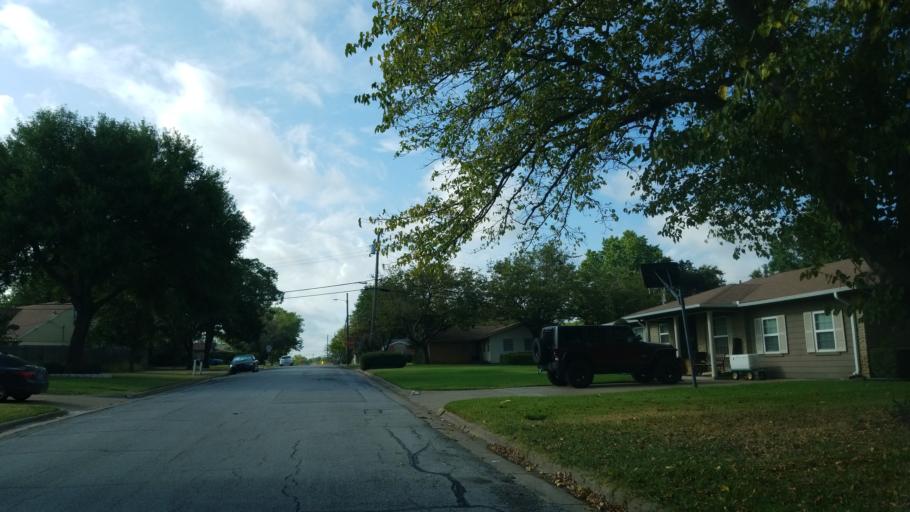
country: US
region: Texas
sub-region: Tarrant County
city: Euless
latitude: 32.8408
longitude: -97.0766
